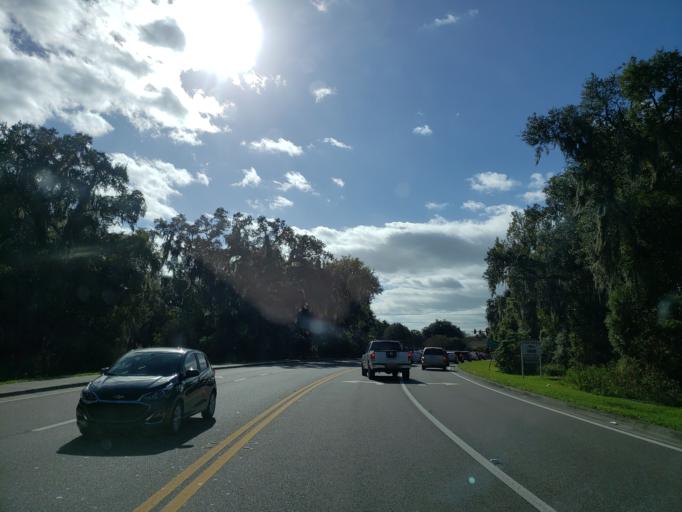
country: US
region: Florida
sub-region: Polk County
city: Medulla
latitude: 27.9763
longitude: -81.9712
